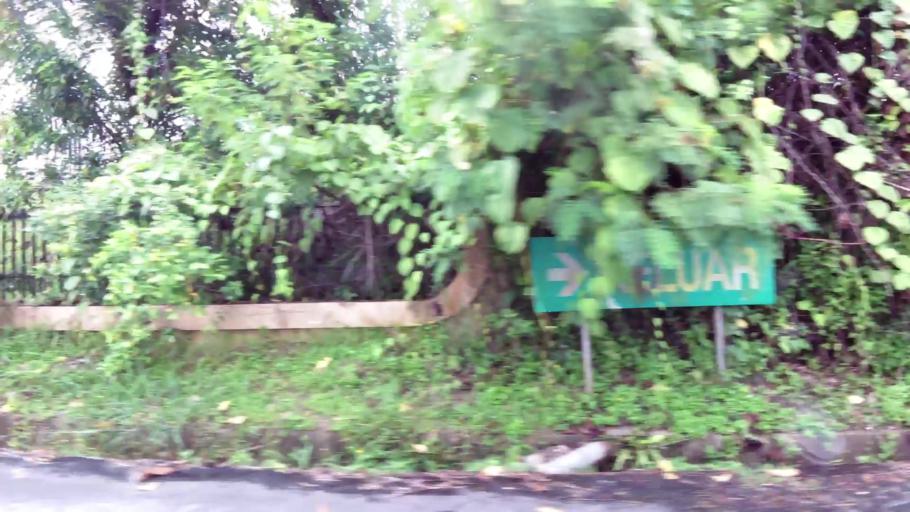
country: BN
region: Brunei and Muara
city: Bandar Seri Begawan
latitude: 4.8949
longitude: 114.9329
